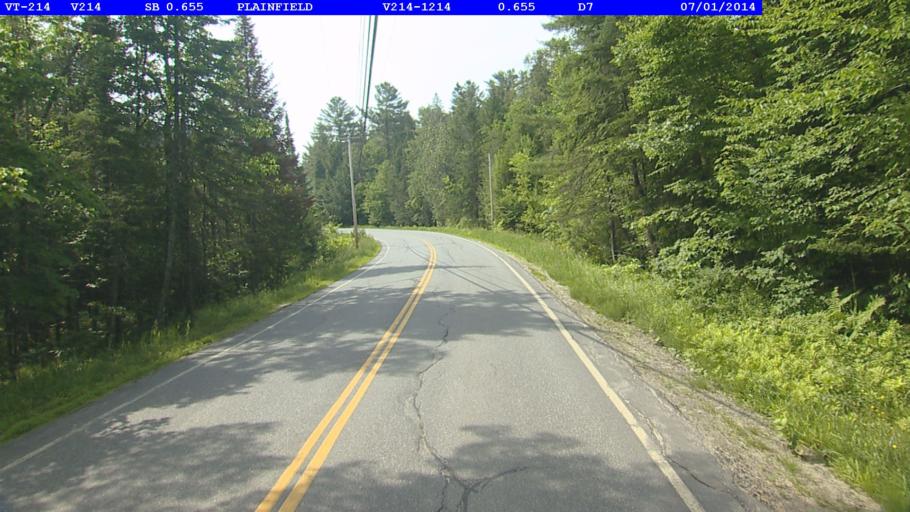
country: US
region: Vermont
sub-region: Washington County
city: Barre
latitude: 44.2861
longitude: -72.4404
